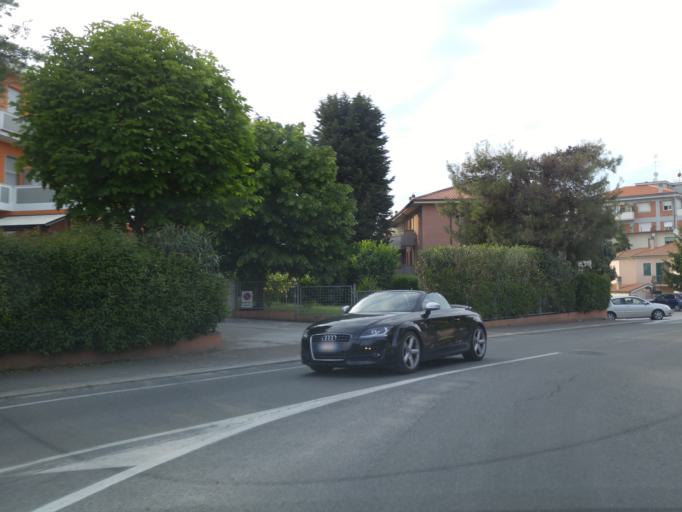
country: IT
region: The Marches
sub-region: Provincia di Ancona
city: Senigallia
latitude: 43.7018
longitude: 13.2191
